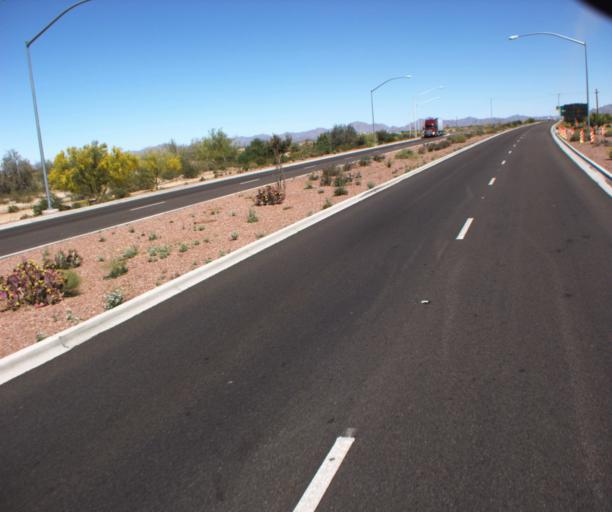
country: US
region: Arizona
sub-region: Maricopa County
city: Gila Bend
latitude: 32.9525
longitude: -112.6929
